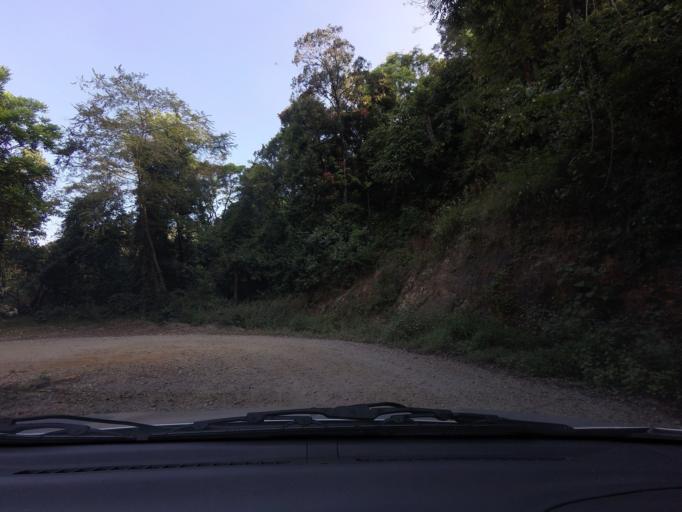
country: IN
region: Karnataka
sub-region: Kodagu
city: Somvarpet
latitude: 12.7130
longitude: 75.6698
